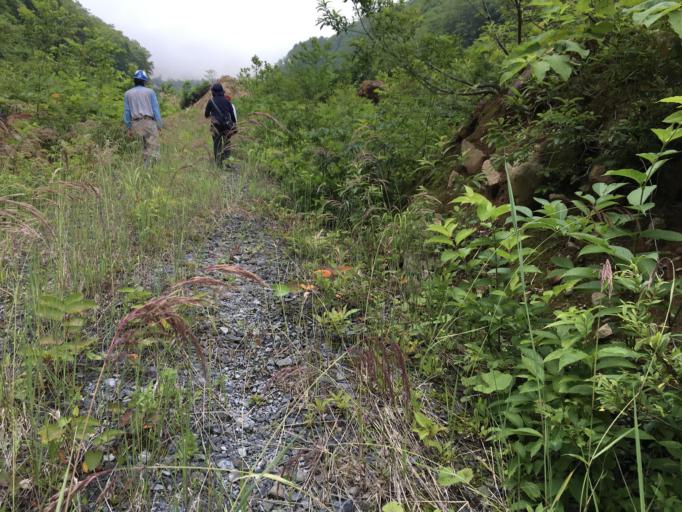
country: JP
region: Iwate
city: Ichinoseki
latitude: 38.9649
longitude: 140.8410
